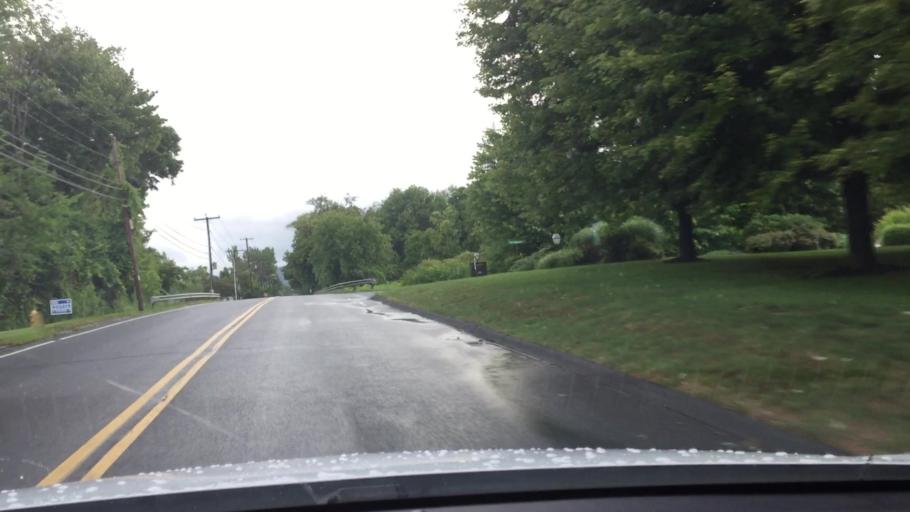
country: US
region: Massachusetts
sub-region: Berkshire County
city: Dalton
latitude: 42.4327
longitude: -73.1964
